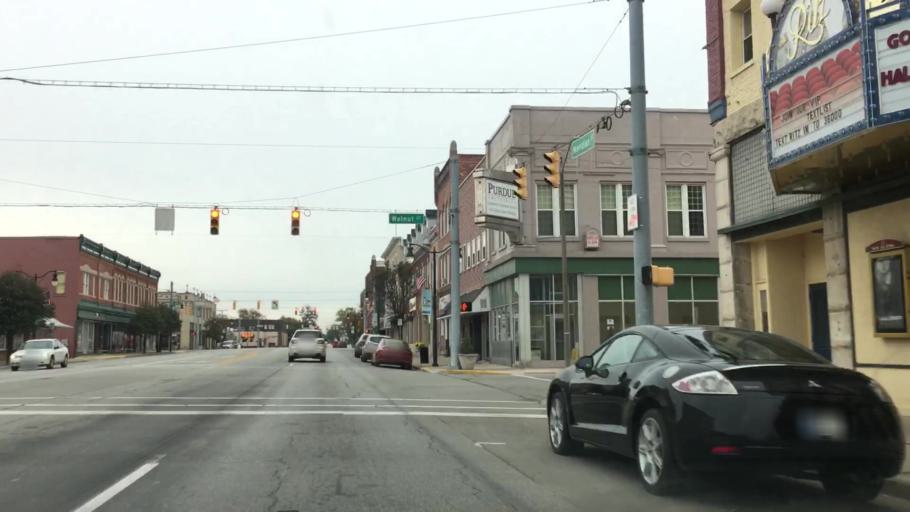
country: US
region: Indiana
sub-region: Jay County
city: Portland
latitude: 40.4346
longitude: -84.9780
